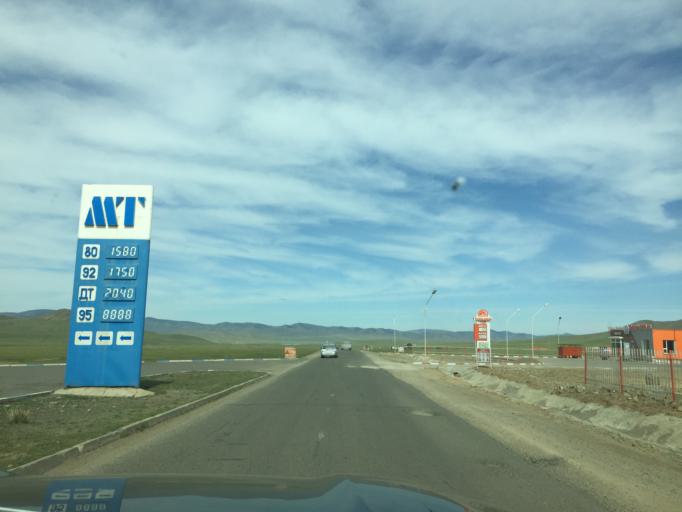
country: MN
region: Central Aimak
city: Ihsueuej
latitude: 48.2289
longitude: 106.2855
